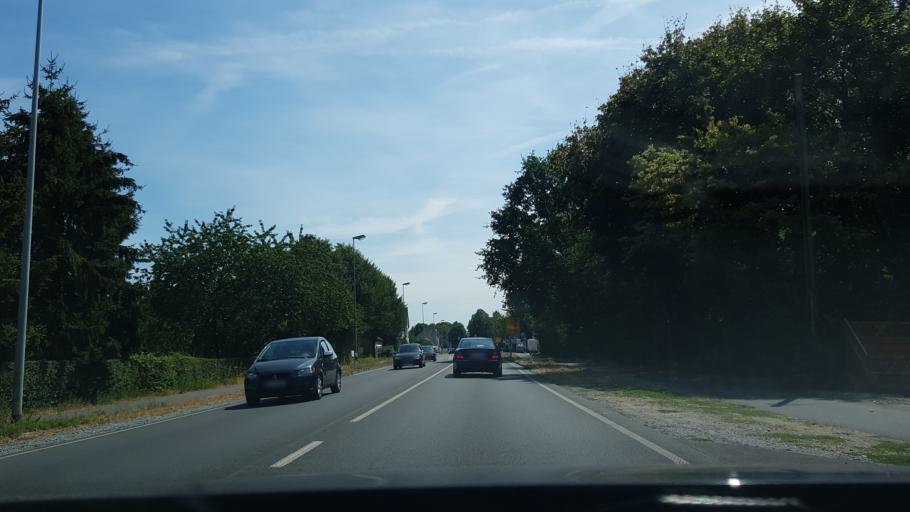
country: DE
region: North Rhine-Westphalia
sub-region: Regierungsbezirk Dusseldorf
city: Dinslaken
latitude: 51.5817
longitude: 6.7235
